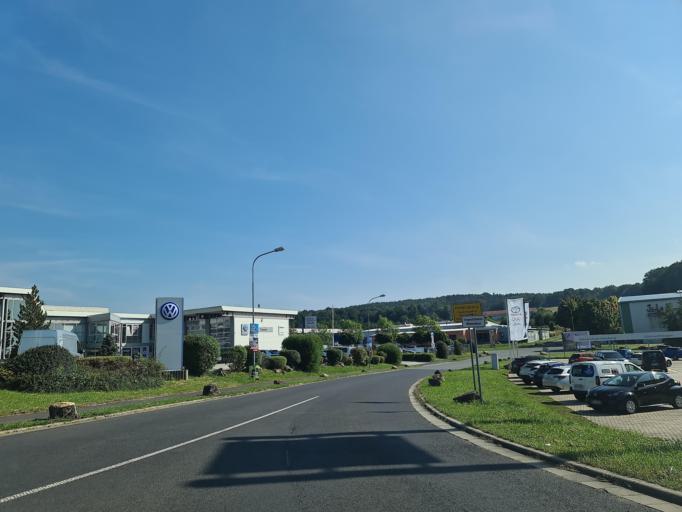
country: DE
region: Thuringia
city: Petersberg
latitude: 50.9696
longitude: 11.8518
